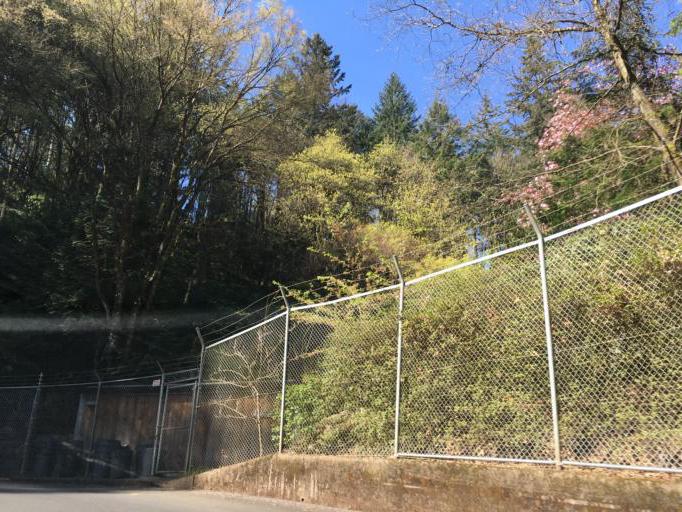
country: US
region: Oregon
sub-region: Multnomah County
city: Portland
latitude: 45.5179
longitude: -122.7082
